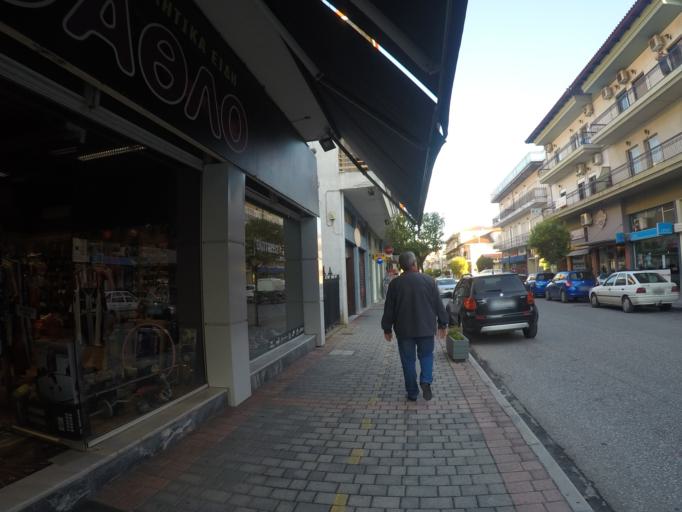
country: GR
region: Thessaly
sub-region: Trikala
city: Kalampaka
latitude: 39.7041
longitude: 21.6291
